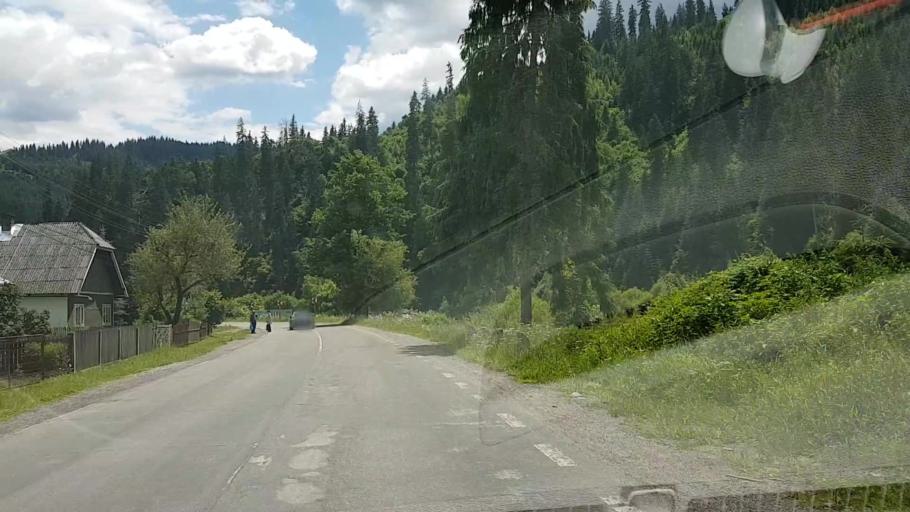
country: RO
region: Suceava
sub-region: Comuna Brosteni
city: Brosteni
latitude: 47.2397
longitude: 25.6913
